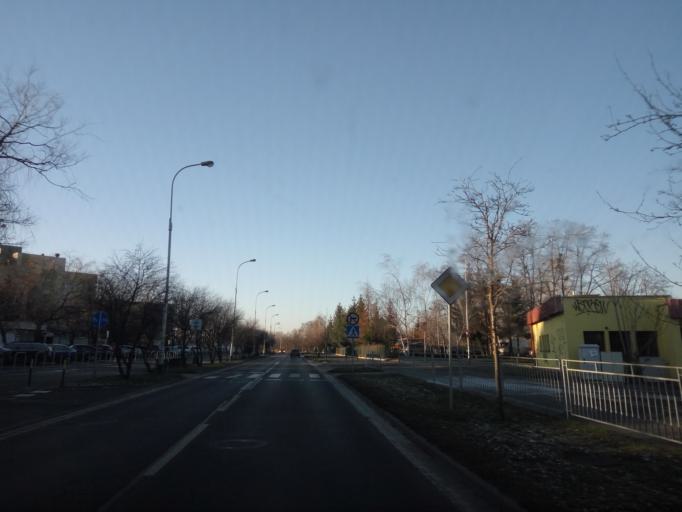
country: PL
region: Lower Silesian Voivodeship
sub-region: Powiat wroclawski
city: Smolec
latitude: 51.1191
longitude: 16.9518
